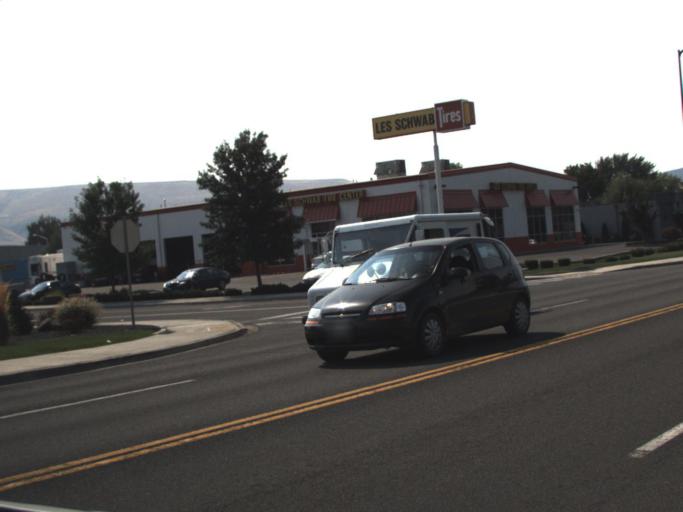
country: US
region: Washington
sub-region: Yakima County
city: Selah
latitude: 46.6596
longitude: -120.5249
